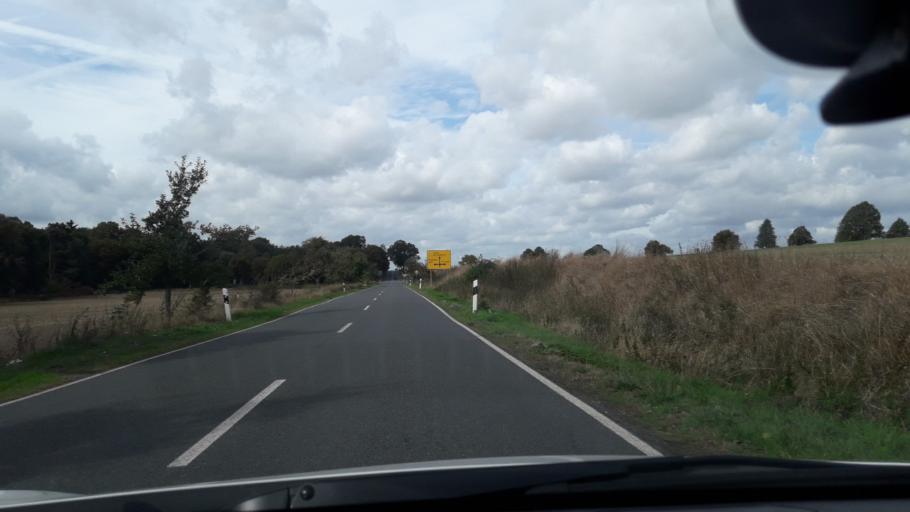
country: DE
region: Lower Saxony
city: Alt Wallmoden
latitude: 52.0260
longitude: 10.3450
